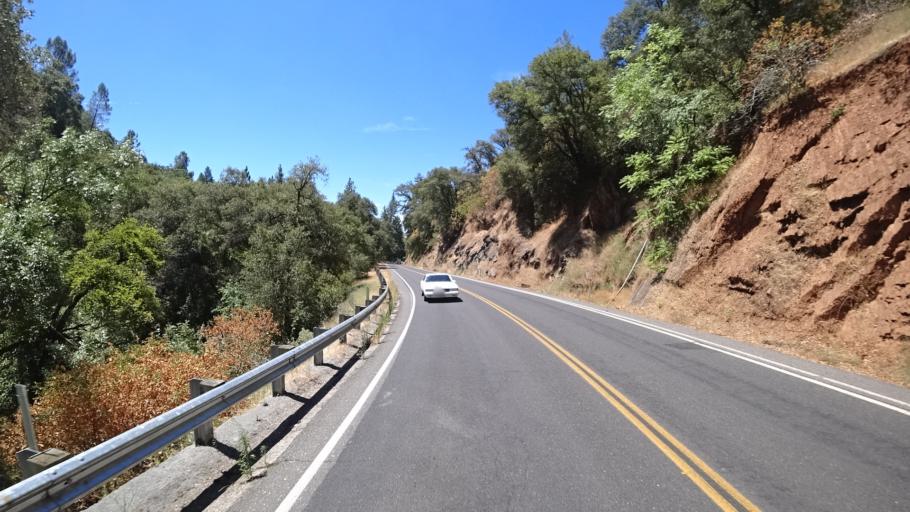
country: US
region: California
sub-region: Calaveras County
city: Murphys
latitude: 38.1239
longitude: -120.4942
